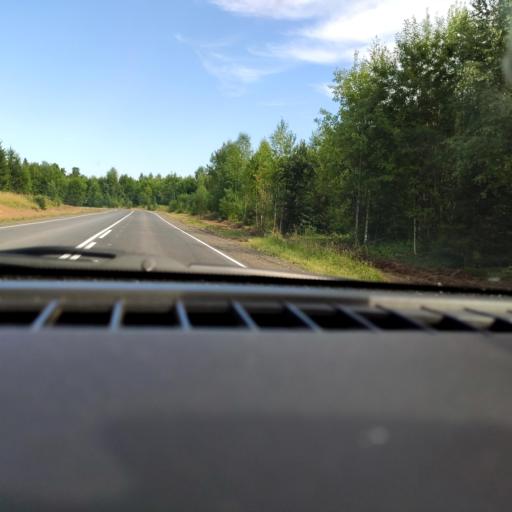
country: RU
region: Perm
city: Polazna
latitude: 58.3346
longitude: 56.1983
